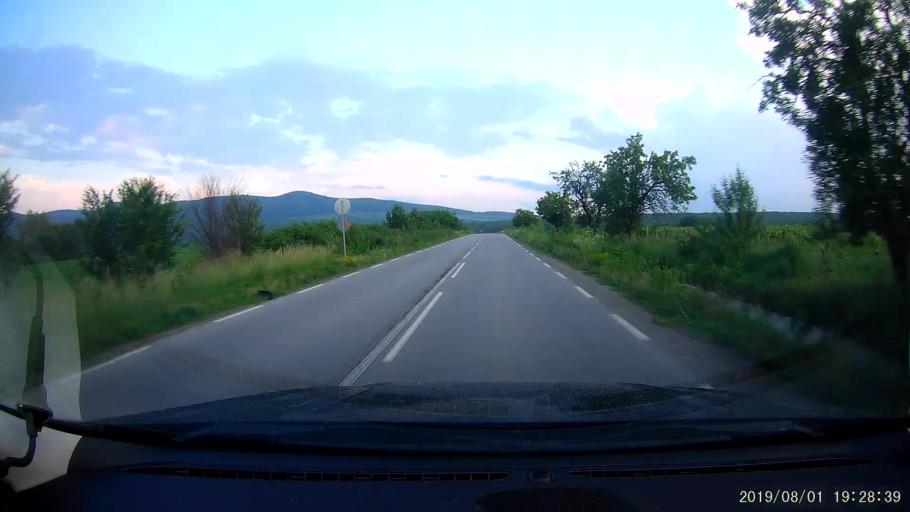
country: BG
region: Burgas
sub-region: Obshtina Sungurlare
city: Sungurlare
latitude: 42.8397
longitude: 26.9143
